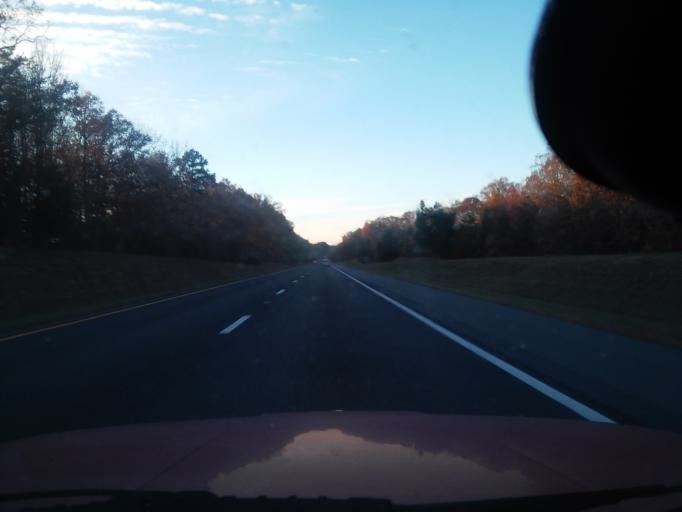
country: US
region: Virginia
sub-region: Louisa County
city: Louisa
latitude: 37.9104
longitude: -78.0630
